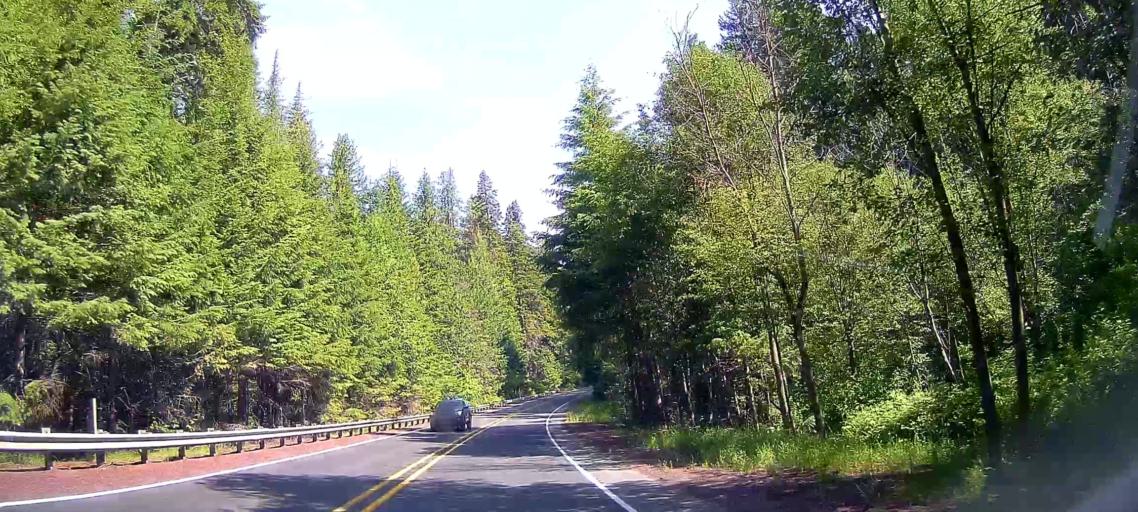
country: US
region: Oregon
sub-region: Jefferson County
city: Warm Springs
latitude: 45.0953
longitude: -121.5528
